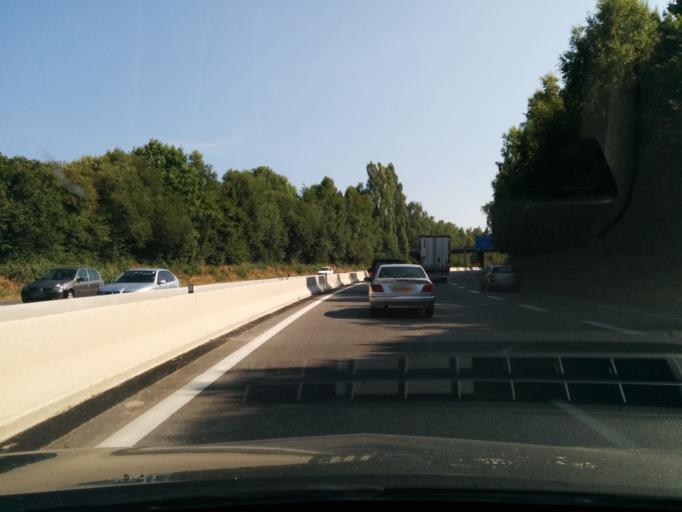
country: FR
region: Limousin
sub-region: Departement de la Haute-Vienne
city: Limoges
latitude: 45.8349
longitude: 1.2843
